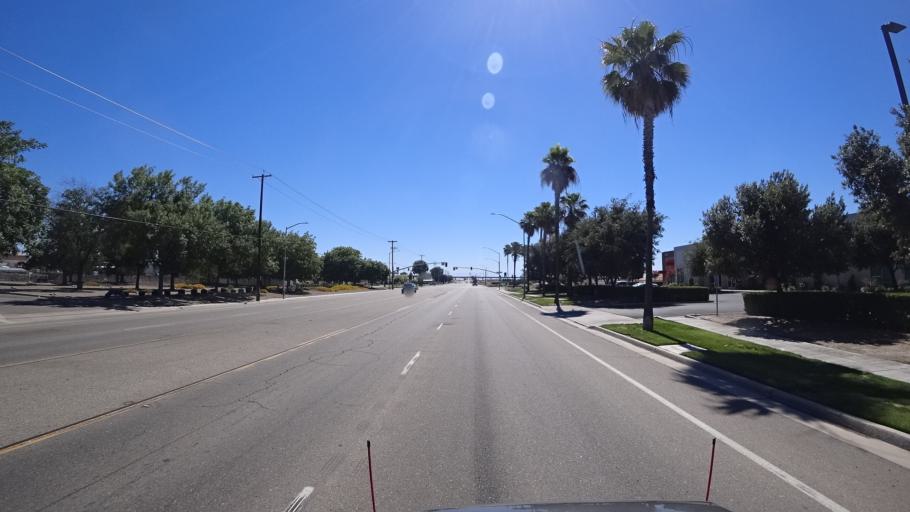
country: US
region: California
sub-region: Fresno County
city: Easton
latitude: 36.6922
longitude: -119.7694
